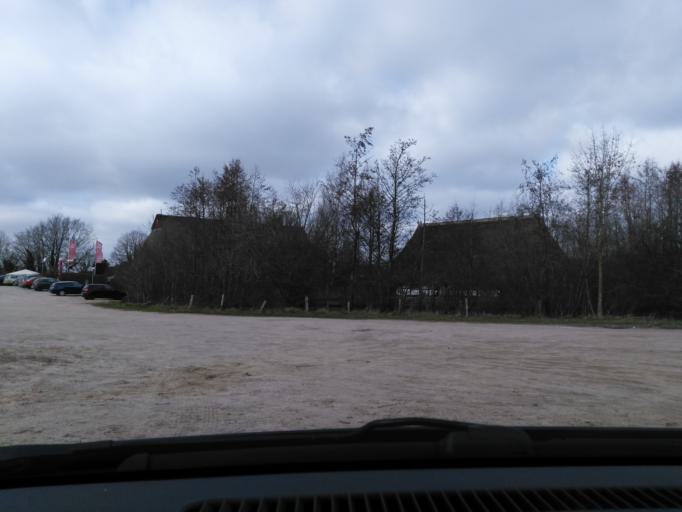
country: DE
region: Schleswig-Holstein
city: Molfsee
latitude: 54.2737
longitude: 10.0769
